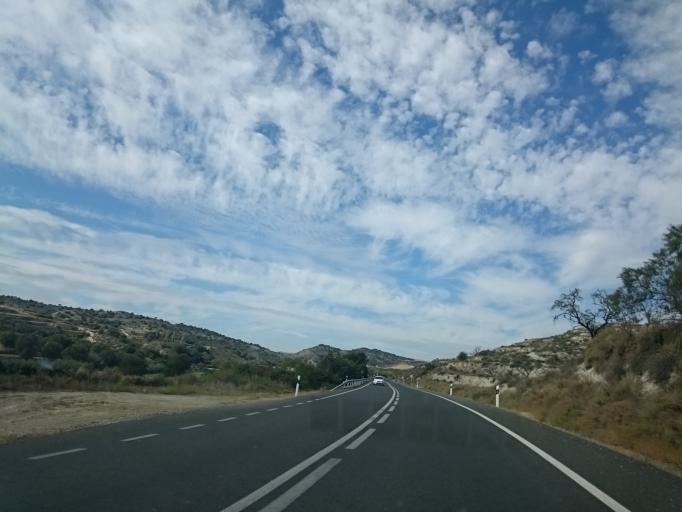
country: ES
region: Aragon
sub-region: Provincia de Huesca
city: Albelda
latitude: 41.8759
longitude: 0.5219
